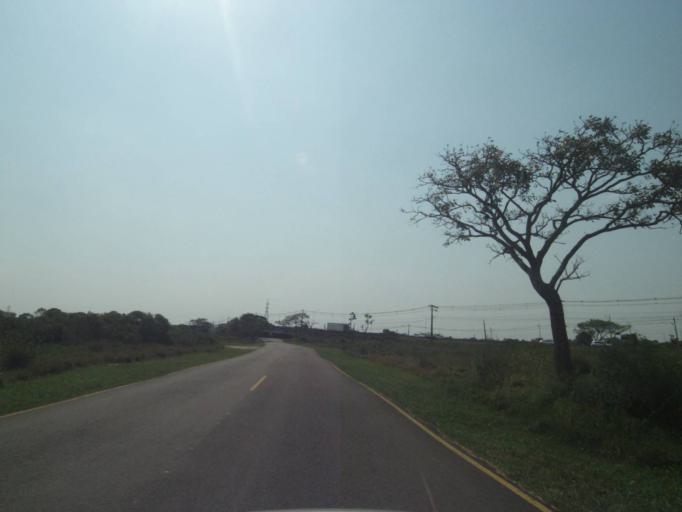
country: BR
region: Parana
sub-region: Sao Jose Dos Pinhais
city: Sao Jose dos Pinhais
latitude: -25.5271
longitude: -49.2240
